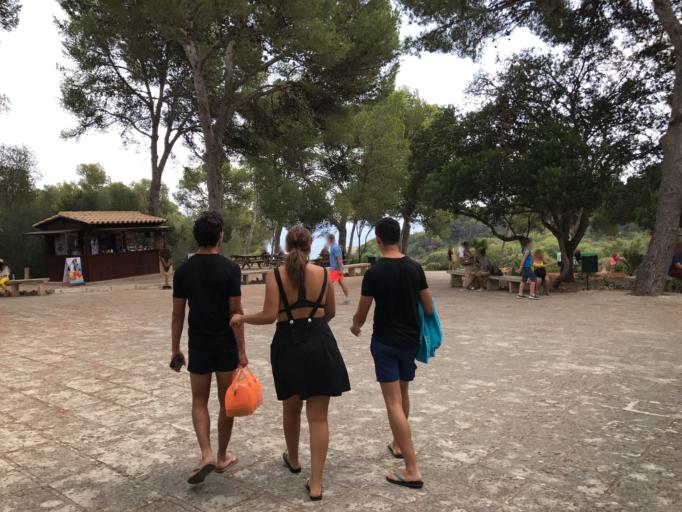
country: ES
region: Balearic Islands
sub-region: Illes Balears
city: Sant Llorenc des Cardassar
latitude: 39.5337
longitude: 3.3312
